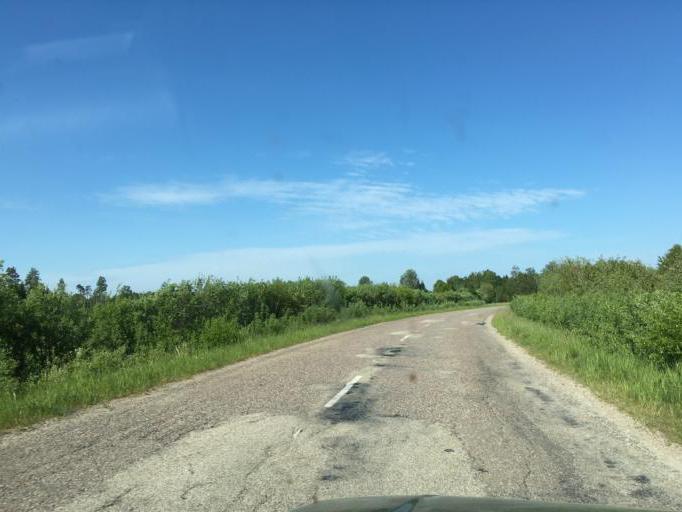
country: LV
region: Ventspils
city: Ventspils
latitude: 57.4992
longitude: 21.8331
